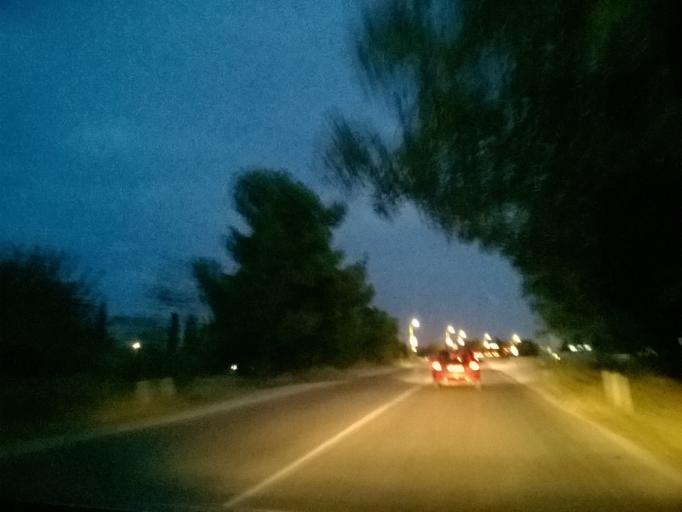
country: ME
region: Podgorica
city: Podgorica
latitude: 42.4430
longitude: 19.2113
